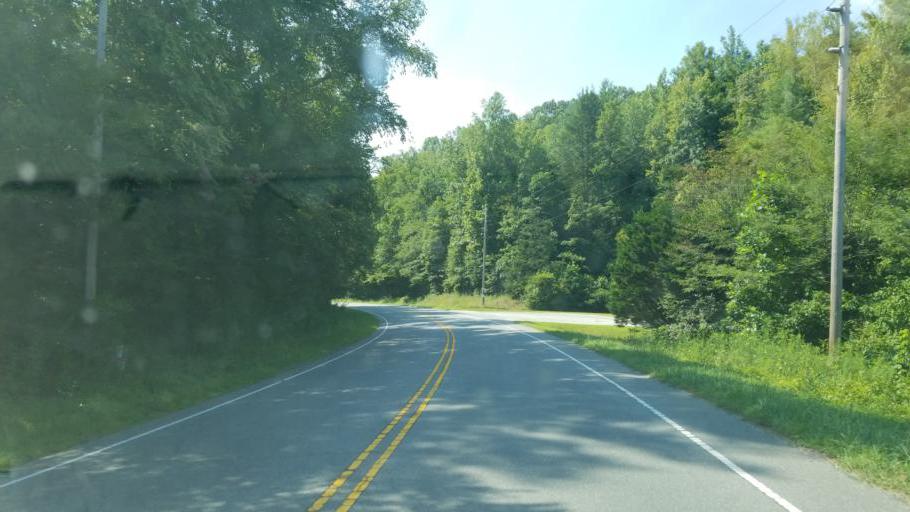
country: US
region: North Carolina
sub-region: Burke County
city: Glen Alpine
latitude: 35.8235
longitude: -81.7937
